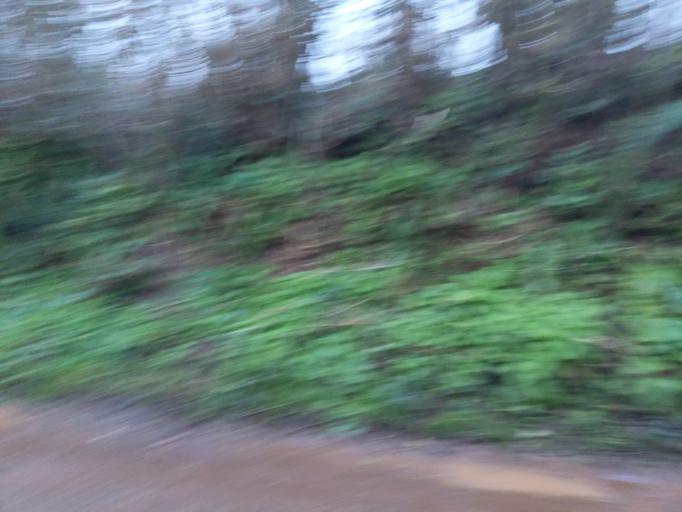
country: GB
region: England
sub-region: Devon
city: Yealmpton
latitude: 50.3259
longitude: -4.0276
